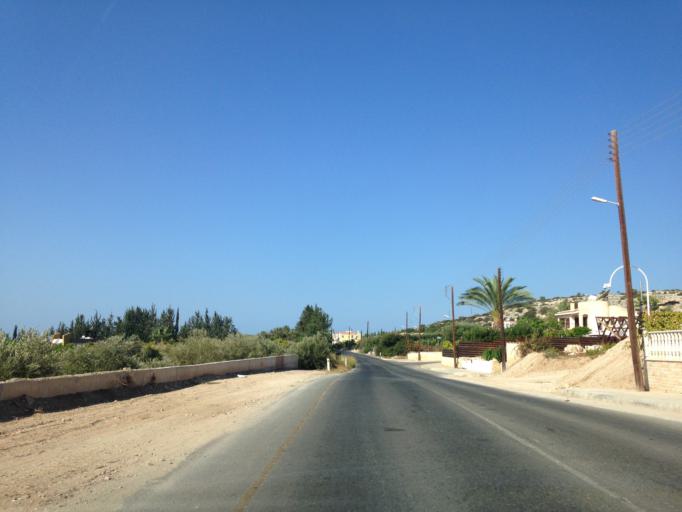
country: CY
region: Pafos
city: Pegeia
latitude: 34.8759
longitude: 32.3654
